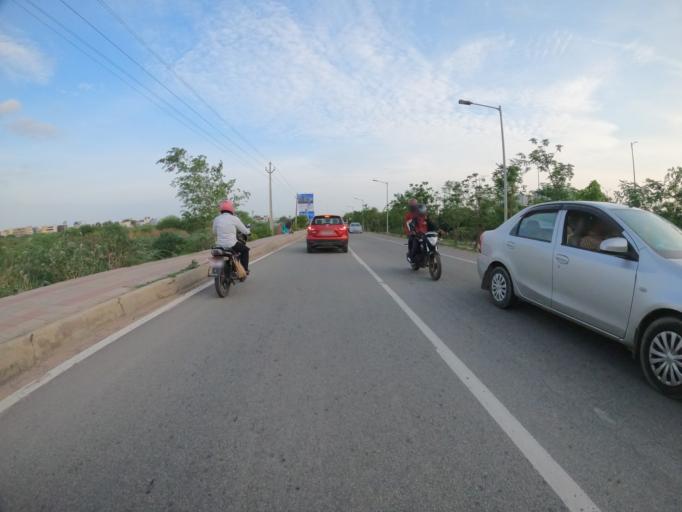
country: IN
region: Telangana
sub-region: Hyderabad
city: Hyderabad
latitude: 17.3935
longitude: 78.3527
